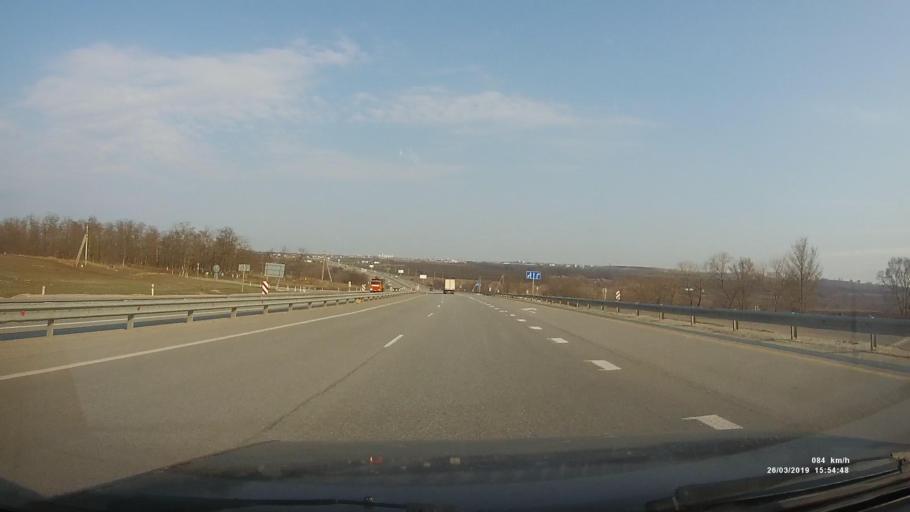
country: RU
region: Rostov
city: Kalinin
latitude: 47.2674
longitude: 39.5641
